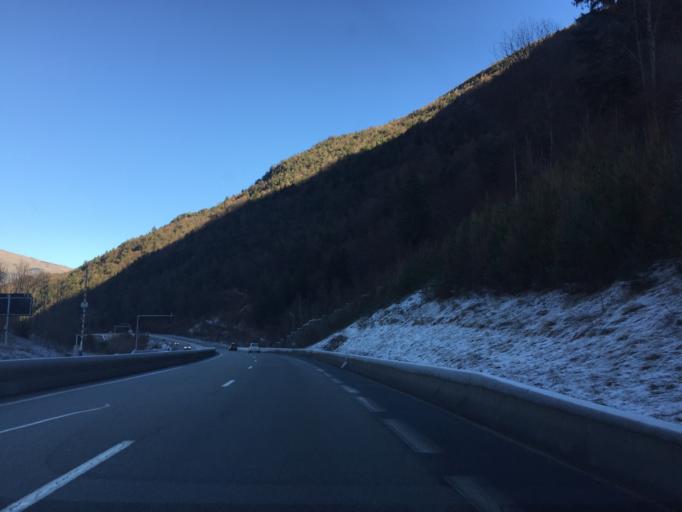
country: FR
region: Rhone-Alpes
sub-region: Departement de la Savoie
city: Aime
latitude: 45.5289
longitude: 6.5933
